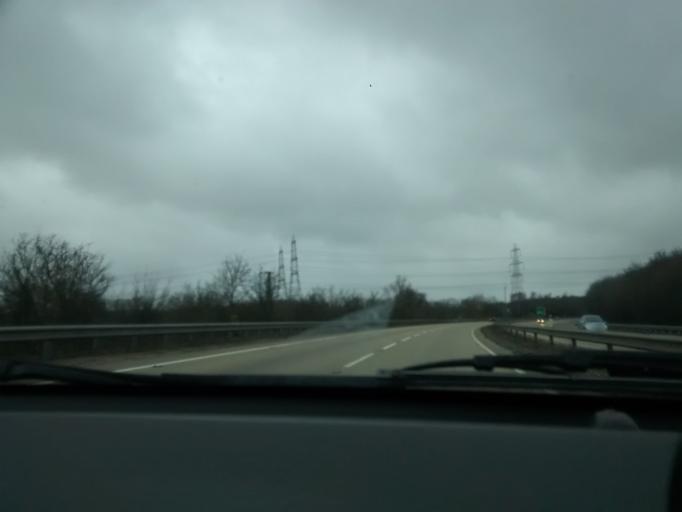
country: GB
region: England
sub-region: Suffolk
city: Bramford
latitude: 52.0822
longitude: 1.1104
